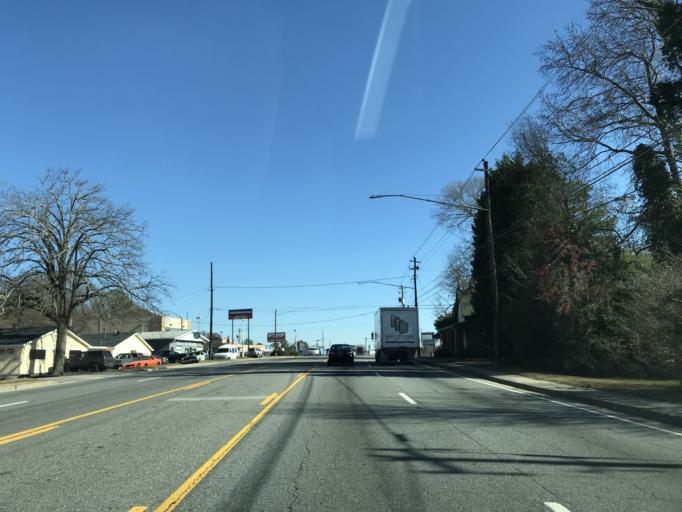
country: US
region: Georgia
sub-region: DeKalb County
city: Tucker
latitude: 33.8498
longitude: -84.2217
